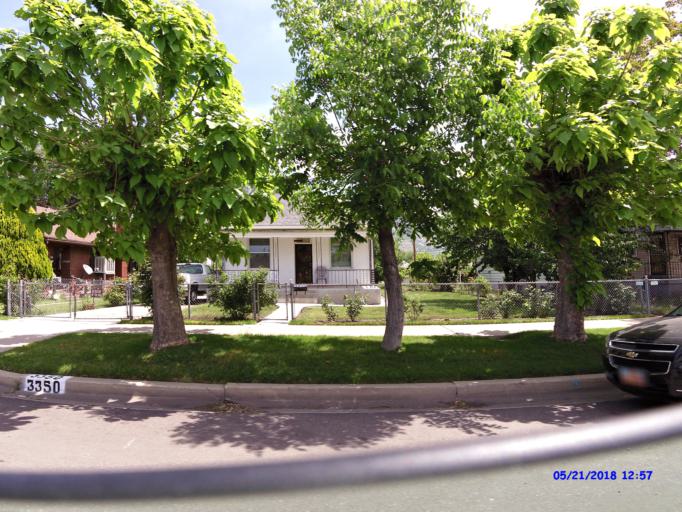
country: US
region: Utah
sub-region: Weber County
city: South Ogden
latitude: 41.2025
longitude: -111.9765
